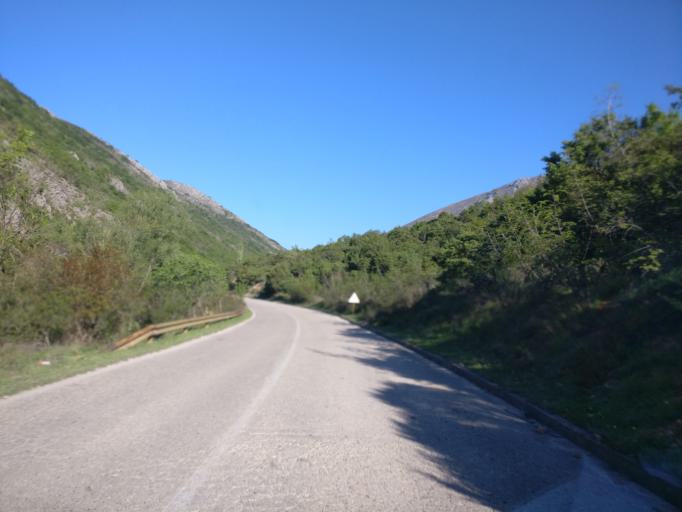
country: BA
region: Federation of Bosnia and Herzegovina
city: Stolac
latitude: 43.0843
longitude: 18.0074
